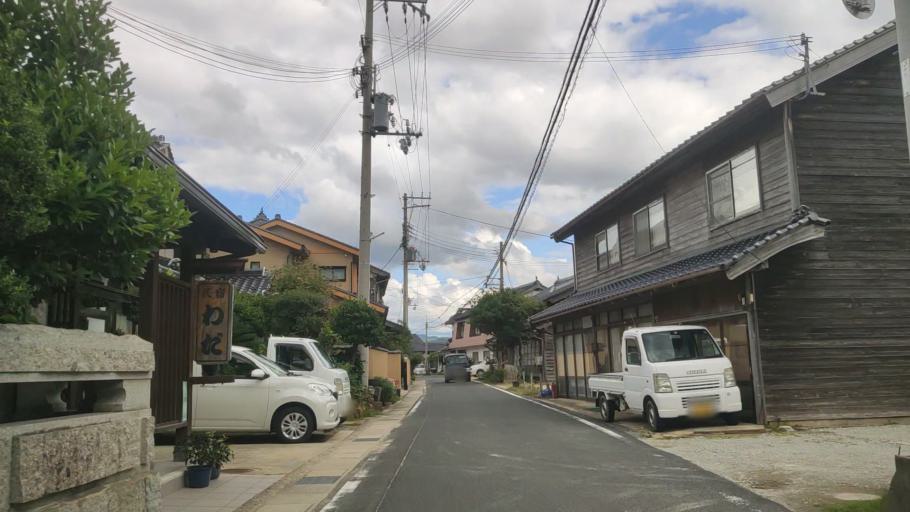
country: JP
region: Hyogo
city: Toyooka
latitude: 35.6427
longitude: 134.9062
